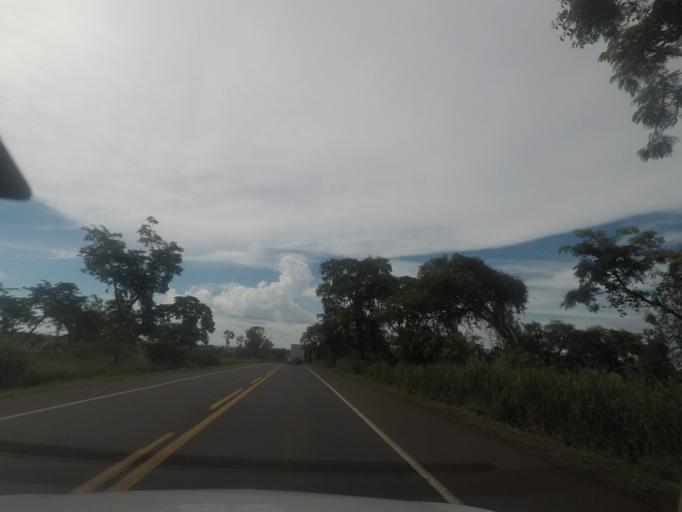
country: BR
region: Minas Gerais
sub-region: Prata
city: Prata
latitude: -19.2475
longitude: -48.9271
